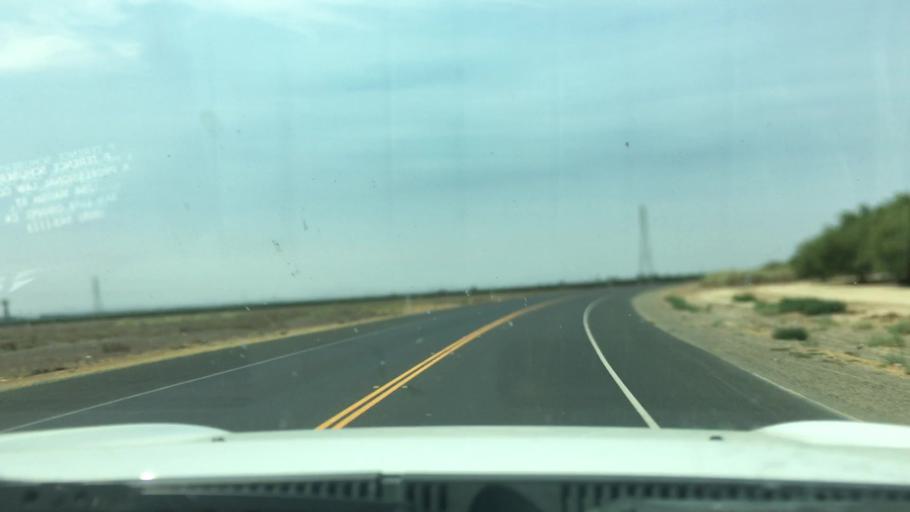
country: US
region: California
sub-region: Kern County
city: Lost Hills
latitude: 35.6021
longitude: -119.5736
